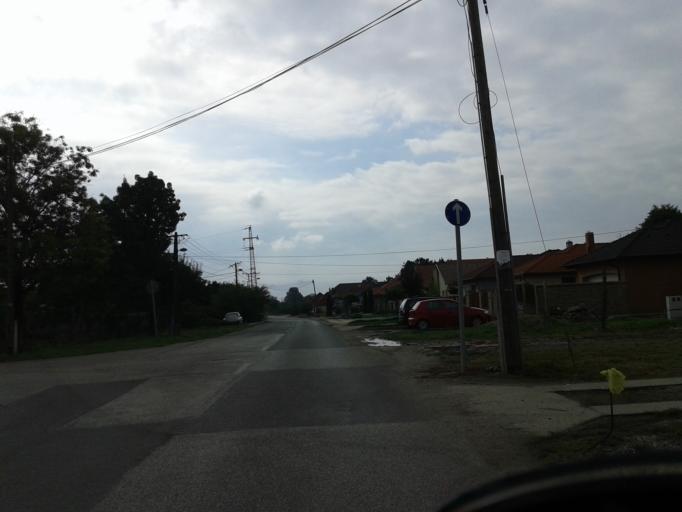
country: HU
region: Csongrad
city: Szeged
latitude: 46.2763
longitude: 20.1176
